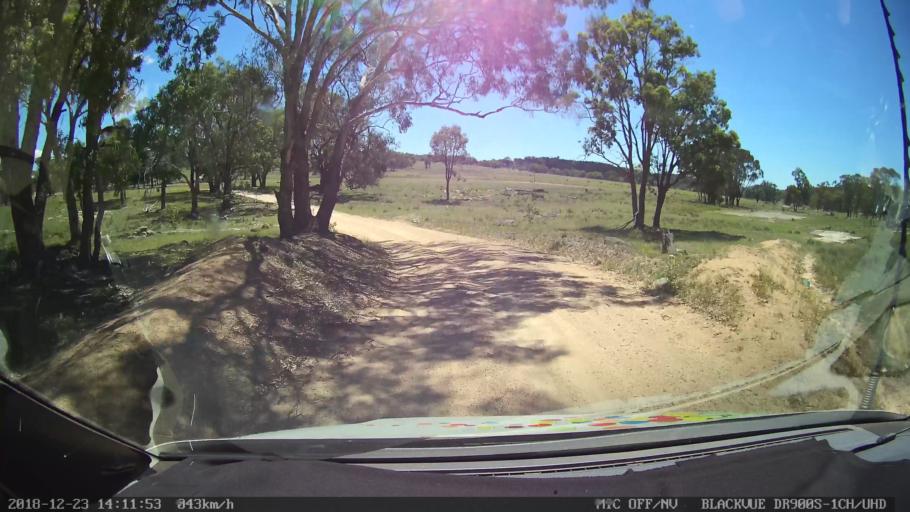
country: AU
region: New South Wales
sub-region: Tamworth Municipality
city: Manilla
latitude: -30.6529
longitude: 151.0478
